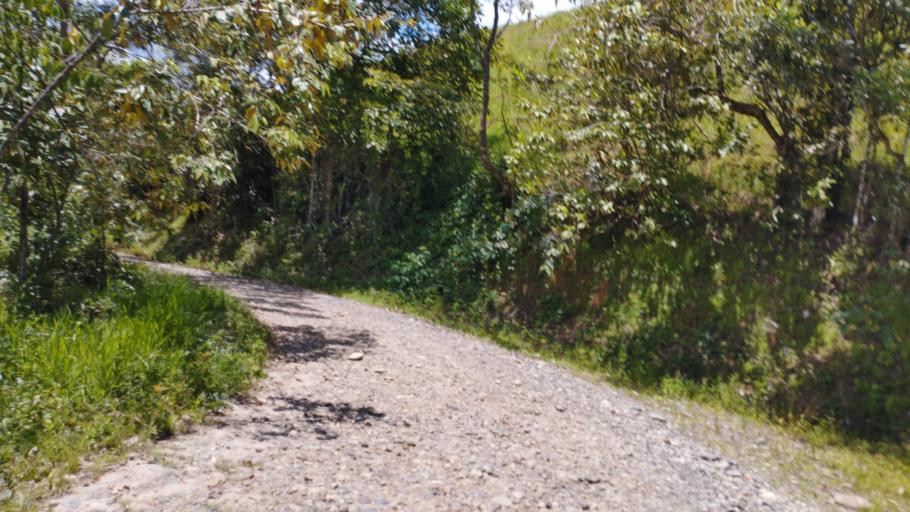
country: CO
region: Boyaca
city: San Luis de Gaceno
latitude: 4.7746
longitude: -73.1347
